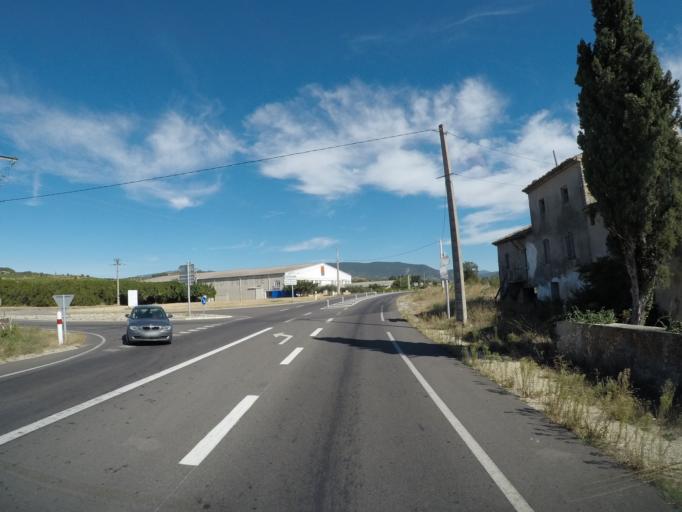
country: FR
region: Rhone-Alpes
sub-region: Departement de la Drome
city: Vinsobres
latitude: 44.3236
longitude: 5.0723
